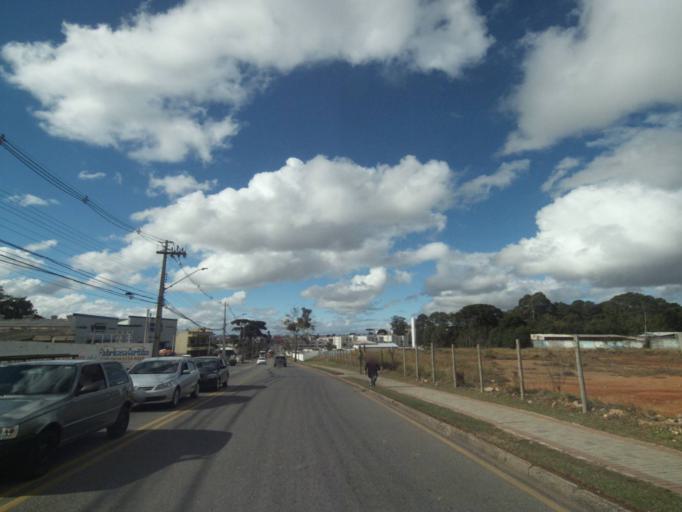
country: BR
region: Parana
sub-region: Sao Jose Dos Pinhais
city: Sao Jose dos Pinhais
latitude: -25.5321
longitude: -49.2971
